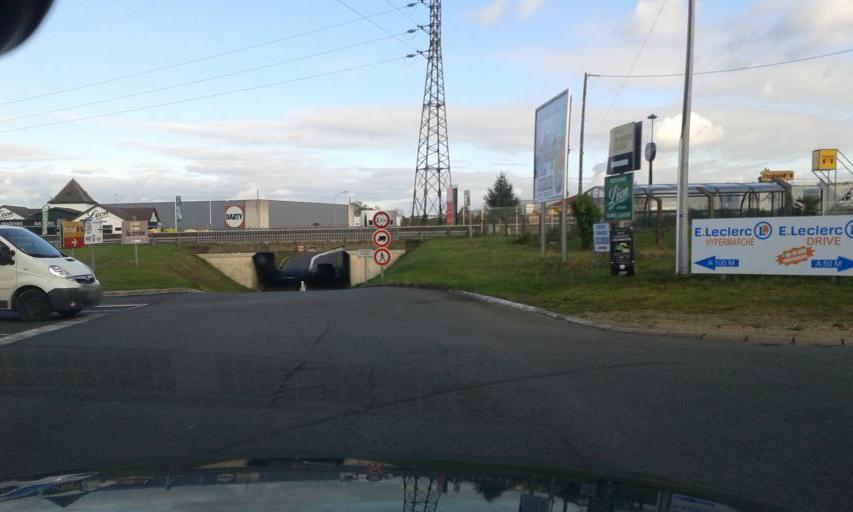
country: FR
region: Centre
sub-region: Departement du Loiret
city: Olivet
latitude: 47.8393
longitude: 1.9135
